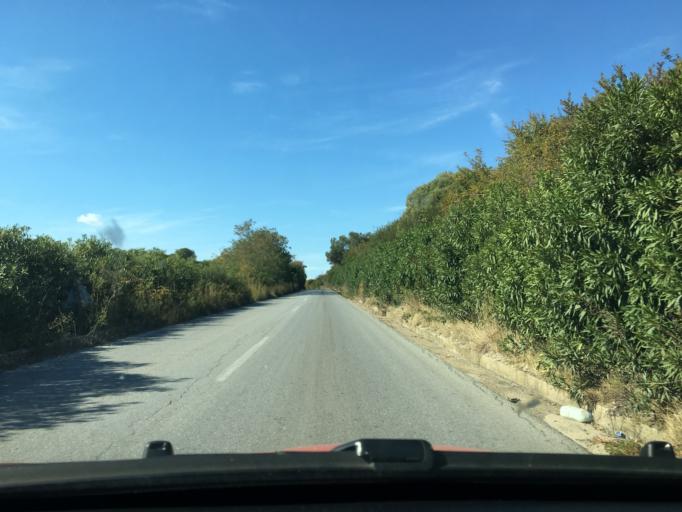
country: GR
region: Central Macedonia
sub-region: Nomos Chalkidikis
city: Nea Roda
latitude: 40.3798
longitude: 23.9094
